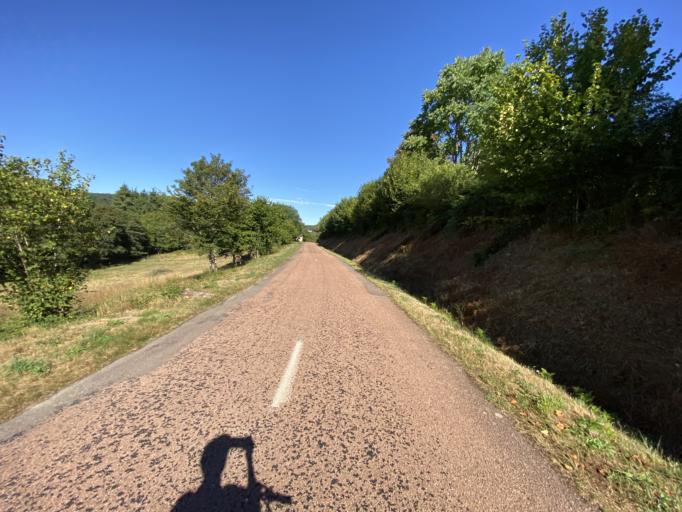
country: FR
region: Bourgogne
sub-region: Departement de la Cote-d'Or
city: Saulieu
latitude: 47.2578
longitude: 4.1840
